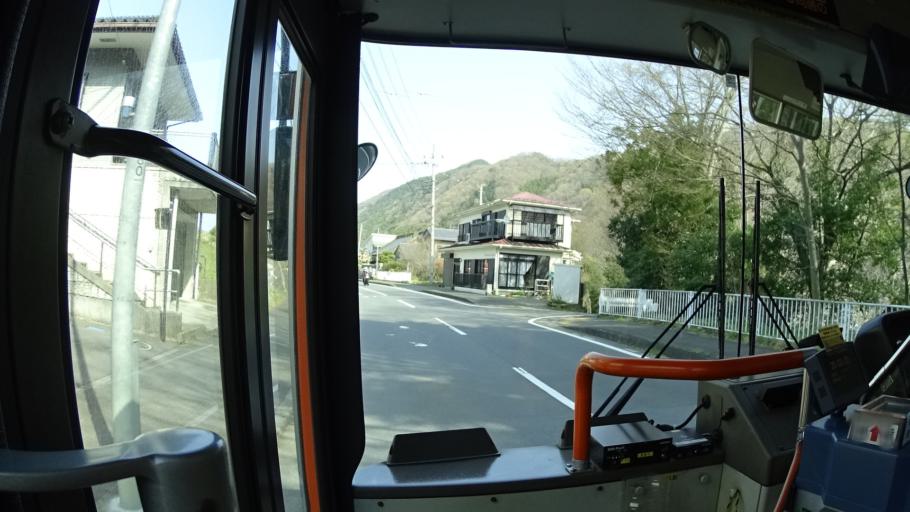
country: JP
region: Kanagawa
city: Atsugi
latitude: 35.4745
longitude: 139.2847
